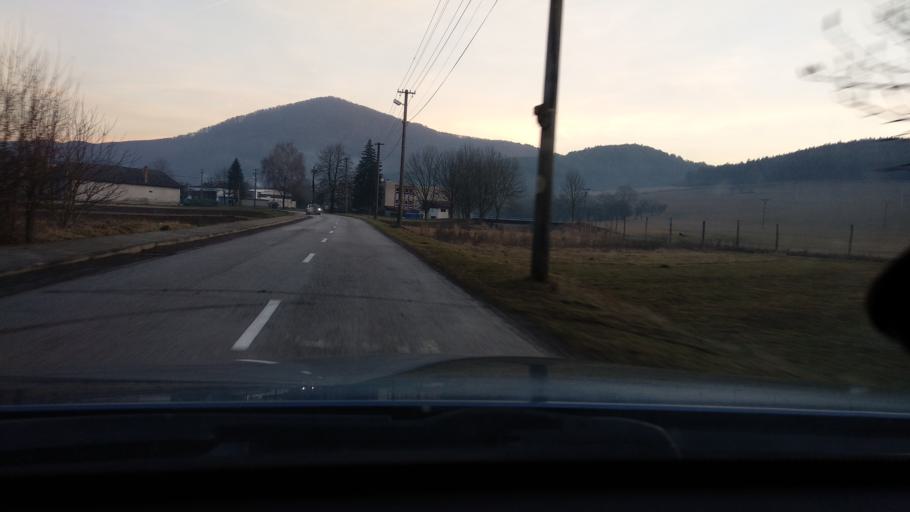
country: SK
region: Nitriansky
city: Trencianske Teplice
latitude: 48.8391
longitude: 18.2603
